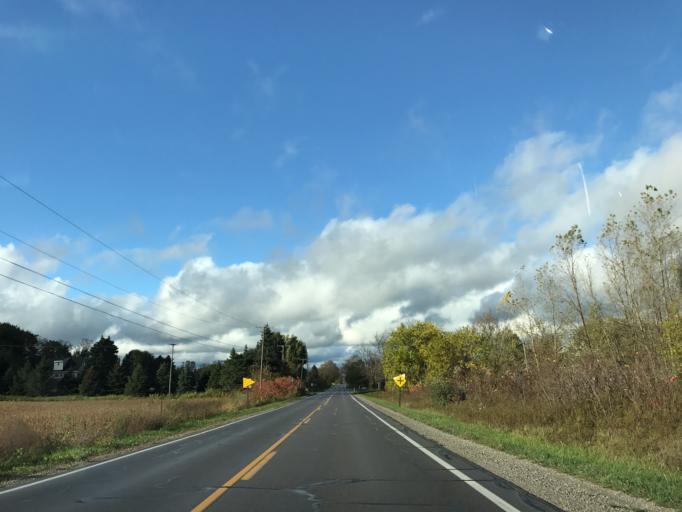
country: US
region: Michigan
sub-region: Oakland County
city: South Lyon
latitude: 42.3857
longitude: -83.6447
